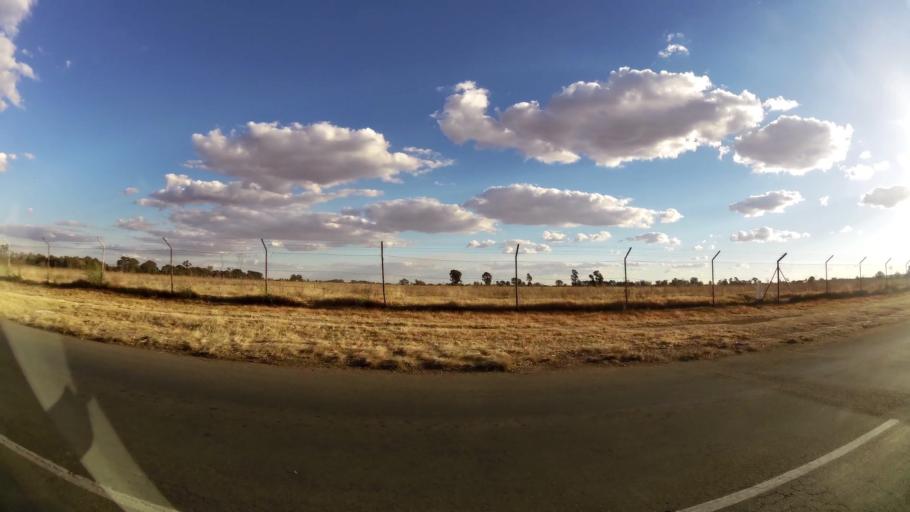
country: ZA
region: North-West
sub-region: Dr Kenneth Kaunda District Municipality
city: Potchefstroom
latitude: -26.7427
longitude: 27.0885
